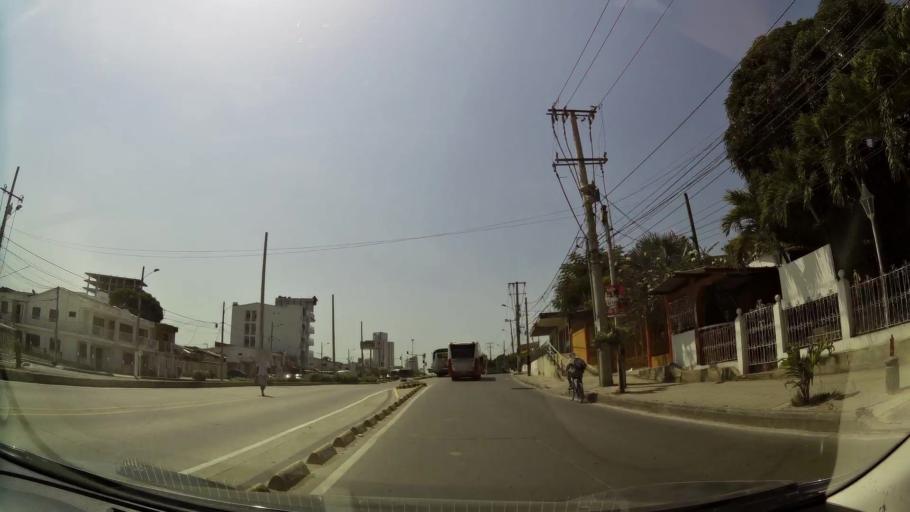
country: CO
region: Bolivar
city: Cartagena
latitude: 10.3969
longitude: -75.4744
